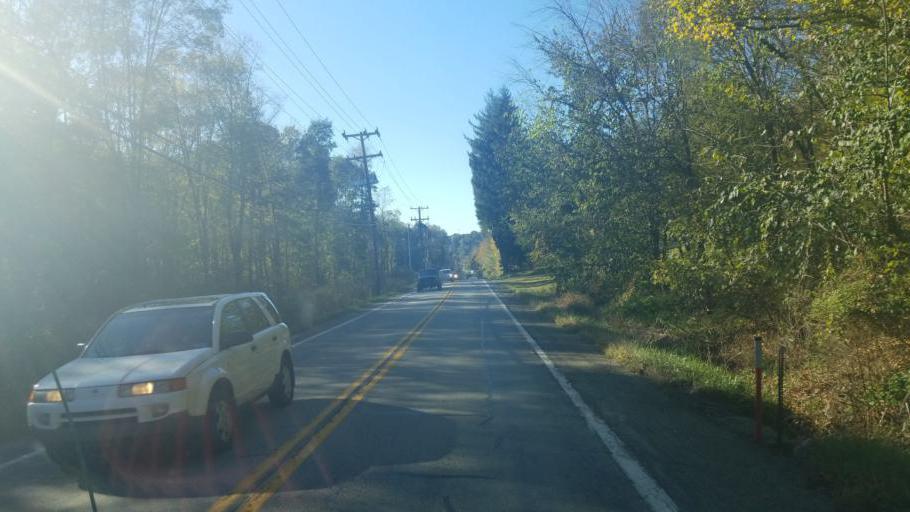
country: US
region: Pennsylvania
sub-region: Allegheny County
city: Imperial
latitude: 40.4960
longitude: -80.3550
